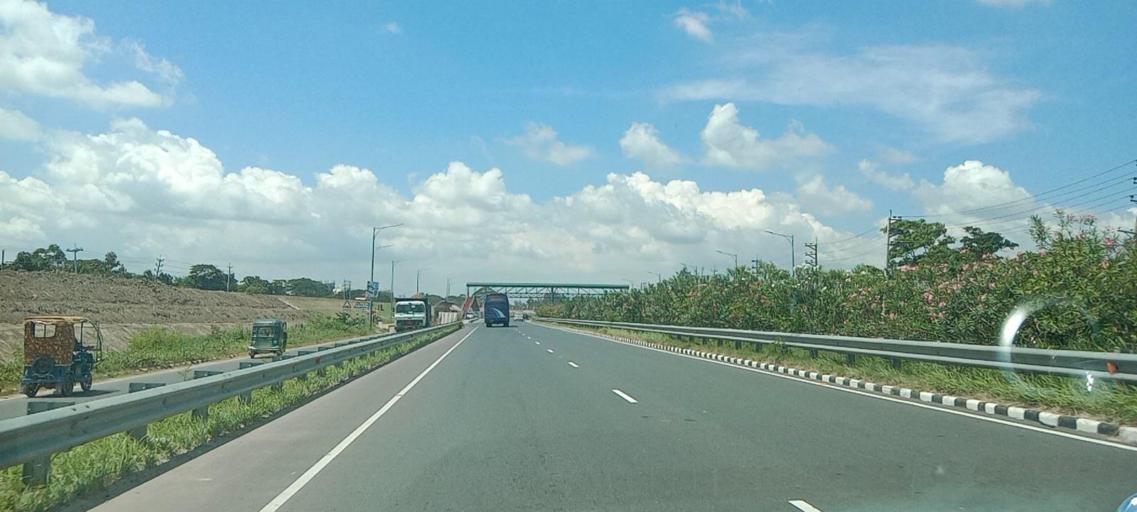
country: BD
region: Dhaka
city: Dohar
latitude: 23.5323
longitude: 90.2904
